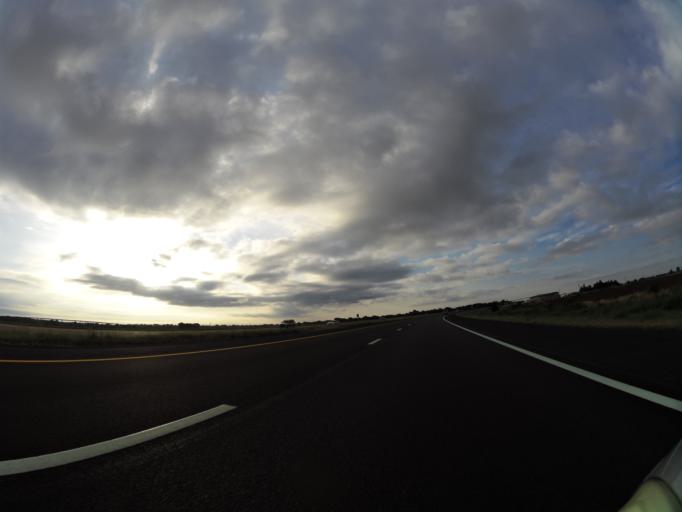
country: US
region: Kansas
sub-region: Sedgwick County
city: Colwich
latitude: 37.8745
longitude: -97.6302
